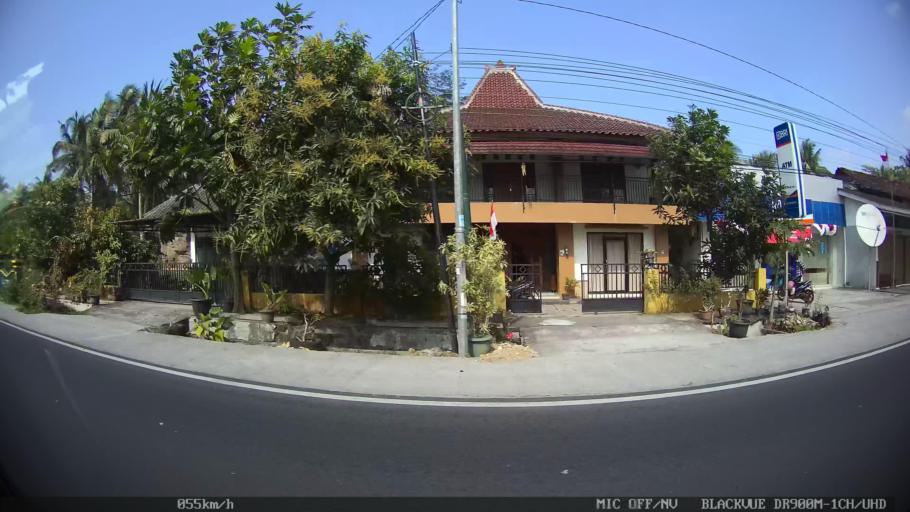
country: ID
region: Daerah Istimewa Yogyakarta
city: Srandakan
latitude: -7.9031
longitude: 110.1682
